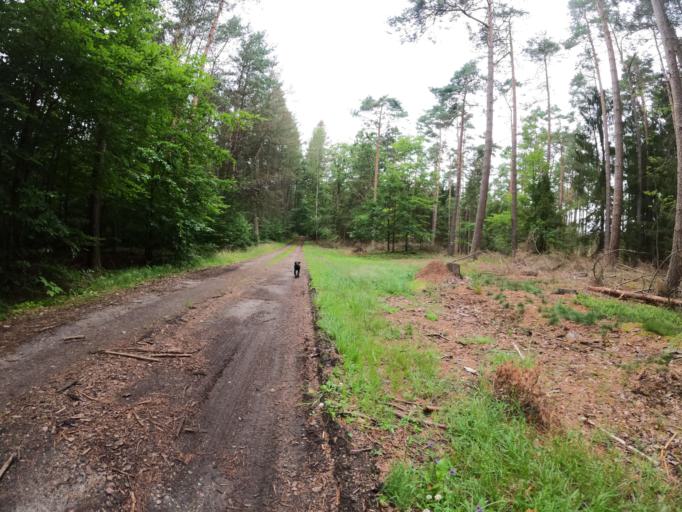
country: PL
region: West Pomeranian Voivodeship
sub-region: Powiat szczecinecki
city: Grzmiaca
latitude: 53.9757
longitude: 16.4252
